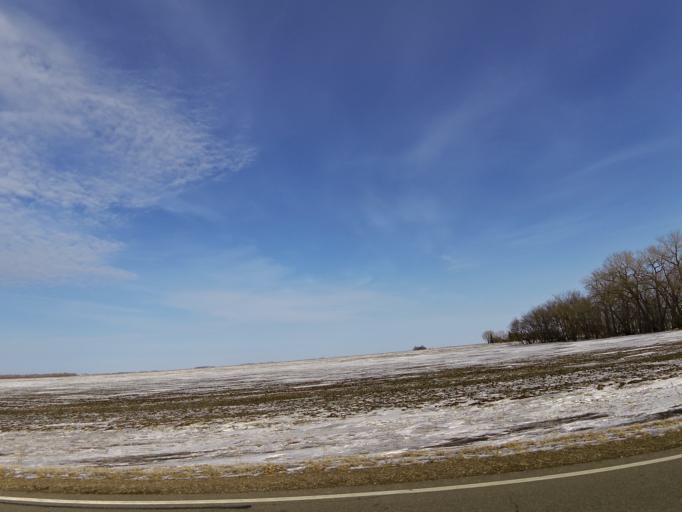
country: US
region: Minnesota
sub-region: Kittson County
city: Hallock
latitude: 48.5604
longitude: -97.1067
